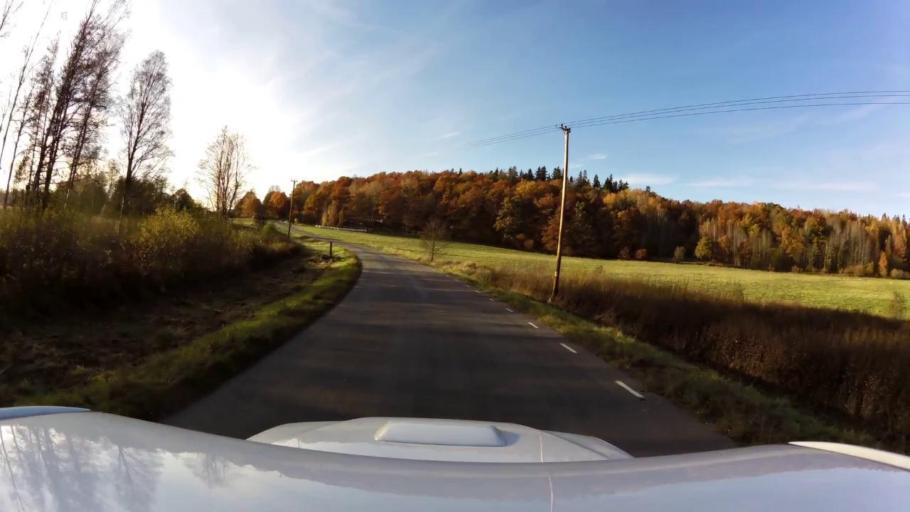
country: SE
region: OEstergoetland
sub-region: Kinda Kommun
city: Rimforsa
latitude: 58.1734
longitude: 15.6857
